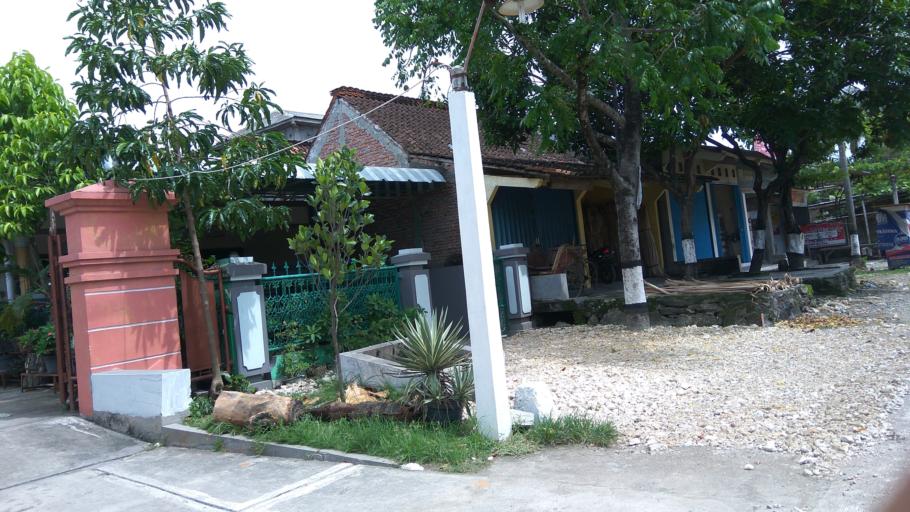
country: ID
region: Central Java
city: Mranggen
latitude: -7.0635
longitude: 110.6662
